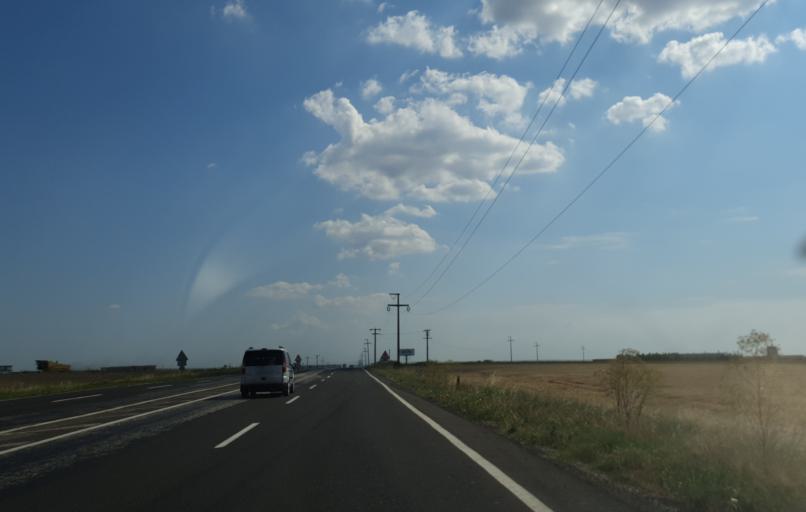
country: TR
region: Kirklareli
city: Buyukkaristiran
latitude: 41.2707
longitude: 27.5519
